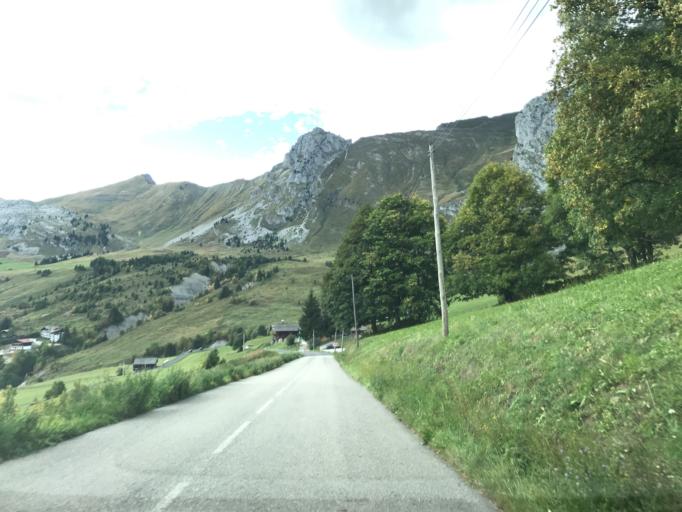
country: FR
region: Rhone-Alpes
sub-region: Departement de la Haute-Savoie
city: Le Grand-Bornand
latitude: 45.9768
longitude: 6.4690
